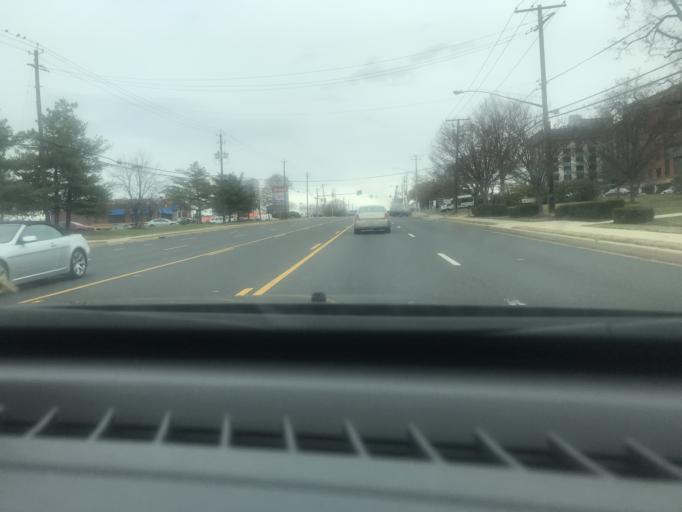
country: US
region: Maryland
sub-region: Prince George's County
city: Oxon Hill
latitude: 38.8040
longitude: -76.9842
